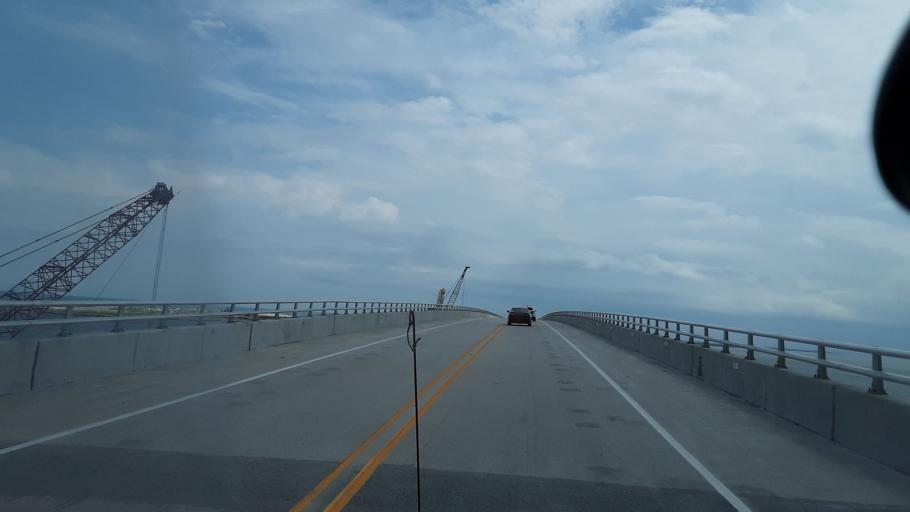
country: US
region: North Carolina
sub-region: Dare County
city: Wanchese
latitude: 35.7738
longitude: -75.5396
